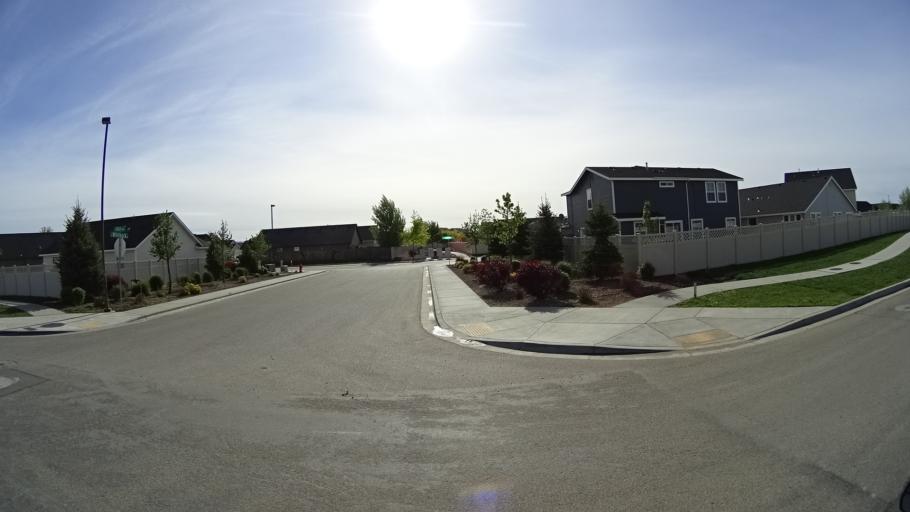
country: US
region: Idaho
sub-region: Ada County
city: Kuna
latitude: 43.5140
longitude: -116.4038
